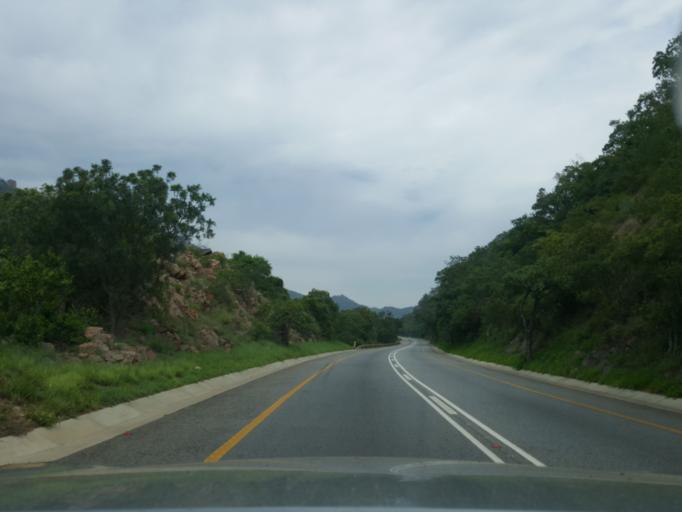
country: ZA
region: Mpumalanga
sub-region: Ehlanzeni District
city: Nelspruit
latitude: -25.5119
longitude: 31.2159
